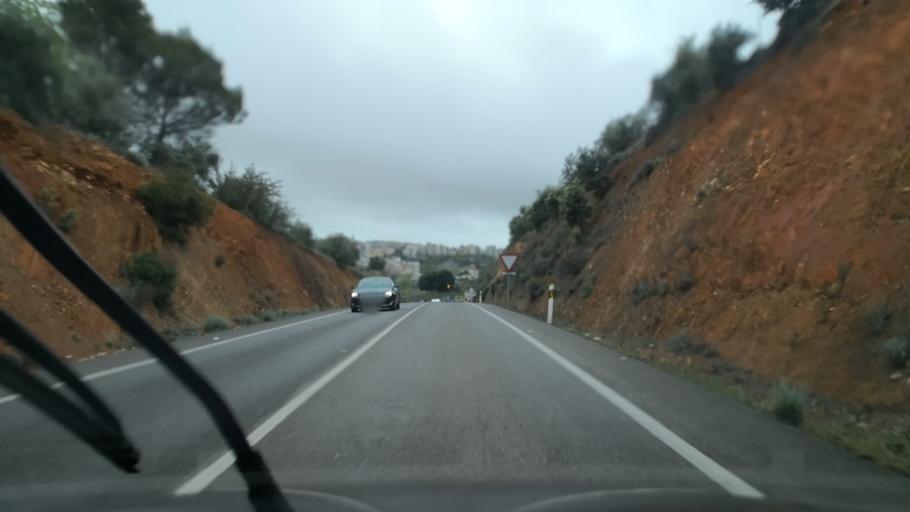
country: ES
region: Extremadura
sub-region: Provincia de Caceres
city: Caceres
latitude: 39.4882
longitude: -6.3832
